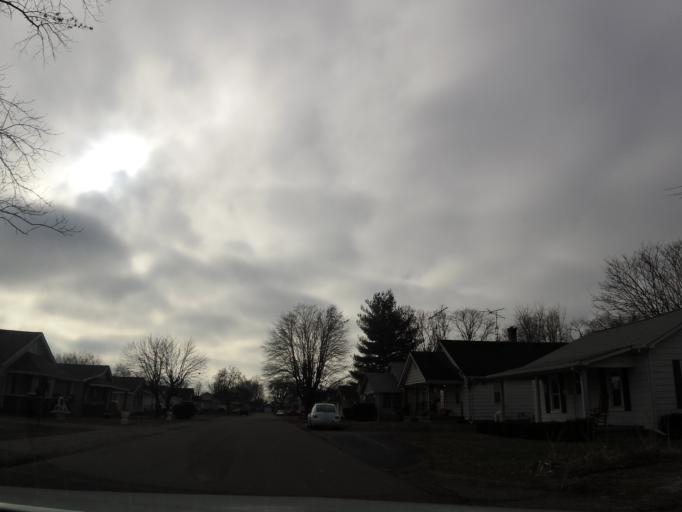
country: US
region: Indiana
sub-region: Bartholomew County
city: Columbus
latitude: 39.2013
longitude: -85.8969
